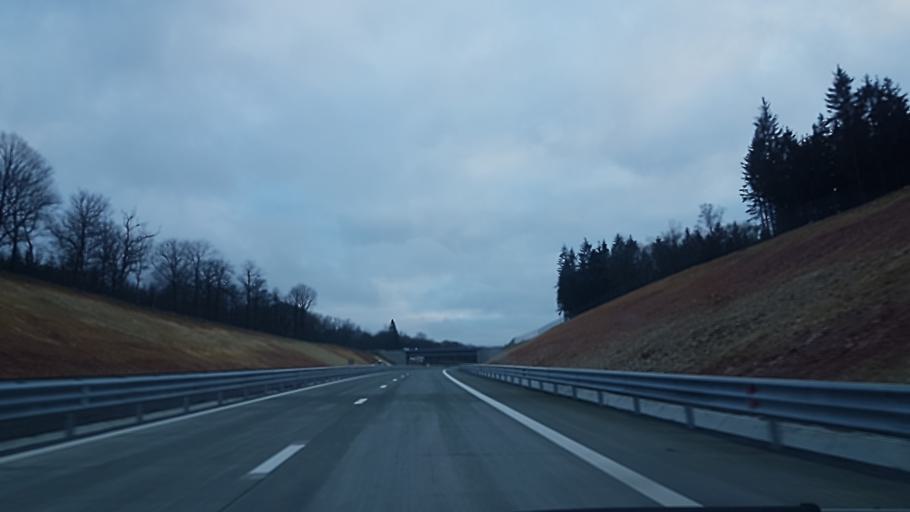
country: BE
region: Wallonia
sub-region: Province de Namur
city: Couvin
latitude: 49.9997
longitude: 4.5419
